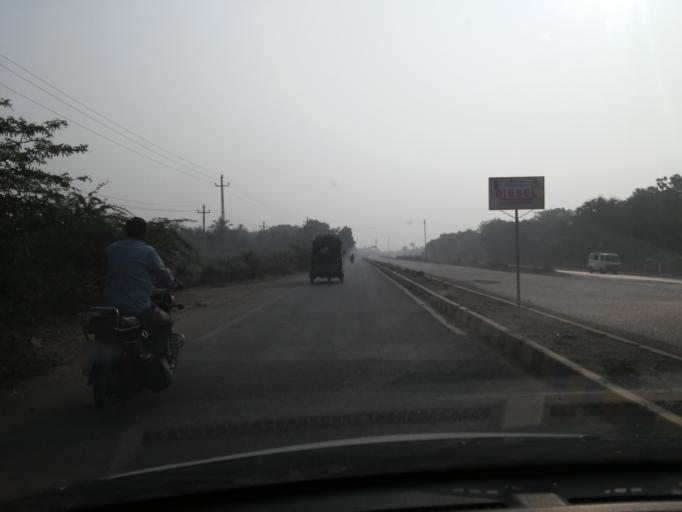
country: IN
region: Gujarat
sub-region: Kachchh
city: Bhuj
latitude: 23.2309
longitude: 69.7536
